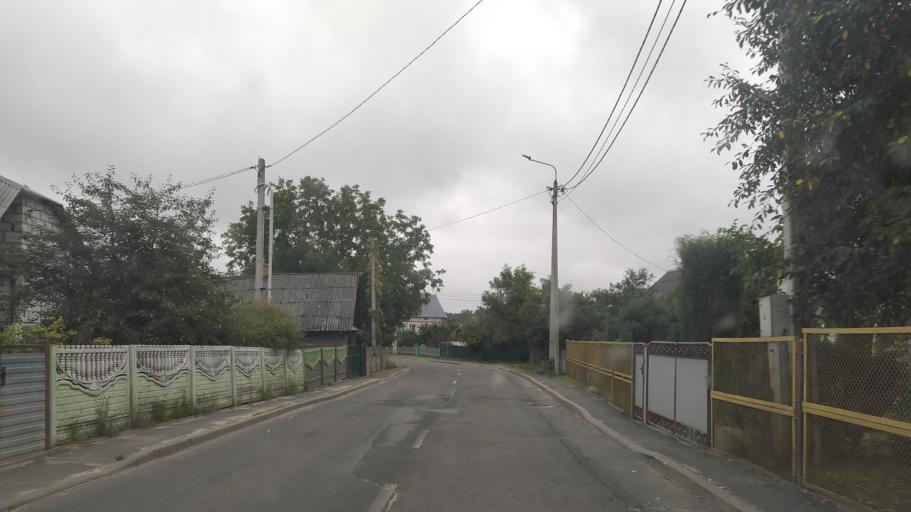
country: BY
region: Brest
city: Byaroza
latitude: 52.5345
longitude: 24.9746
